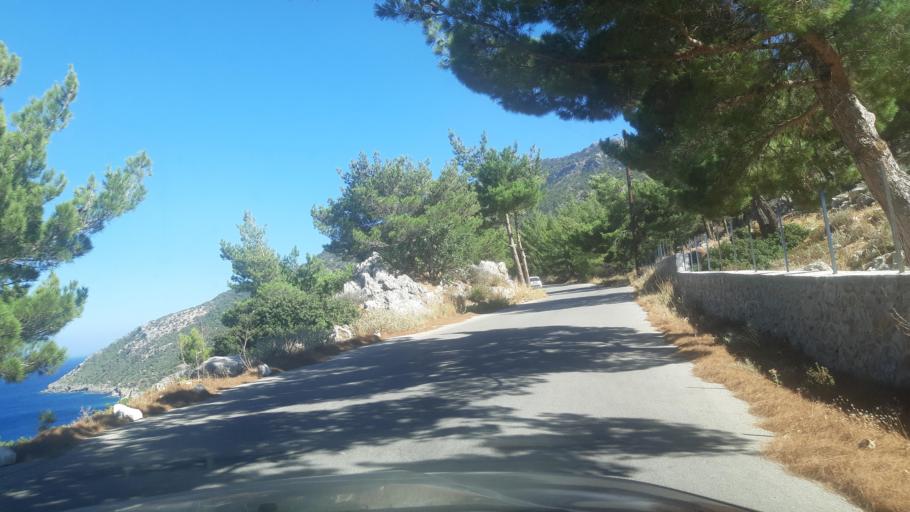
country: GR
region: South Aegean
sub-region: Nomos Dodekanisou
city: Karpathos
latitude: 35.5855
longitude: 27.1787
